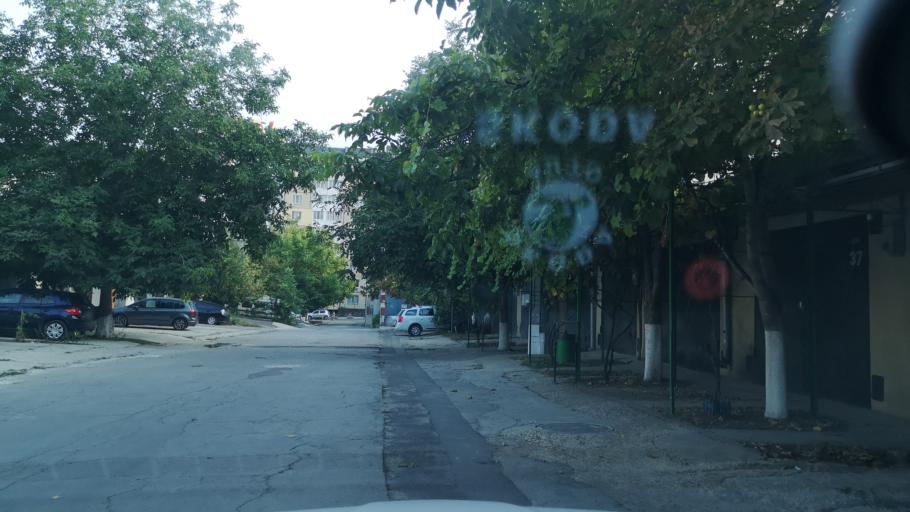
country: MD
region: Chisinau
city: Stauceni
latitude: 47.0490
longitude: 28.8926
